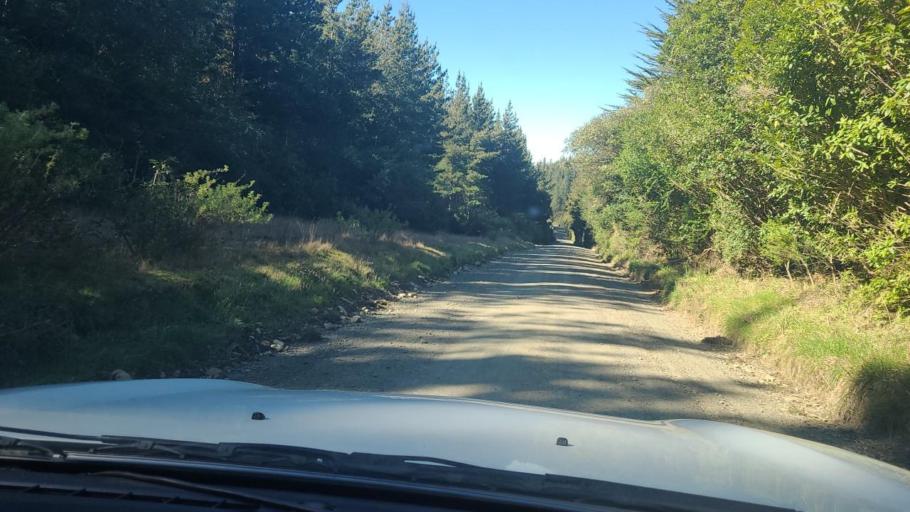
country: NZ
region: Hawke's Bay
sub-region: Napier City
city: Taradale
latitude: -39.4066
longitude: 176.4608
